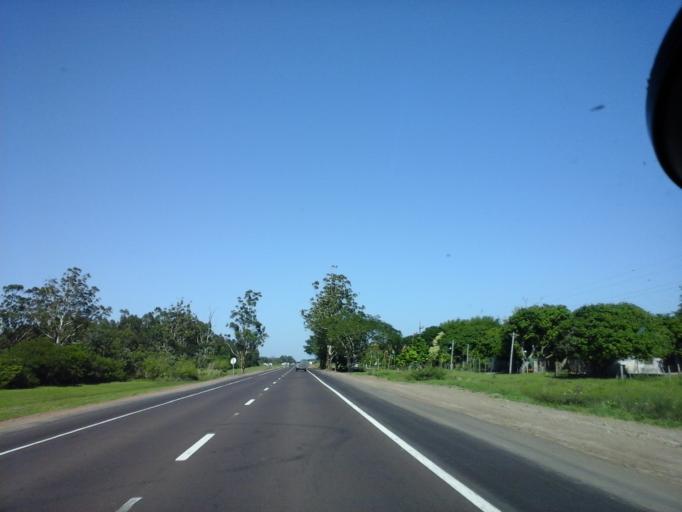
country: AR
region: Corrientes
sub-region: Departamento de San Cosme
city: San Cosme
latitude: -27.3674
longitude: -58.3656
